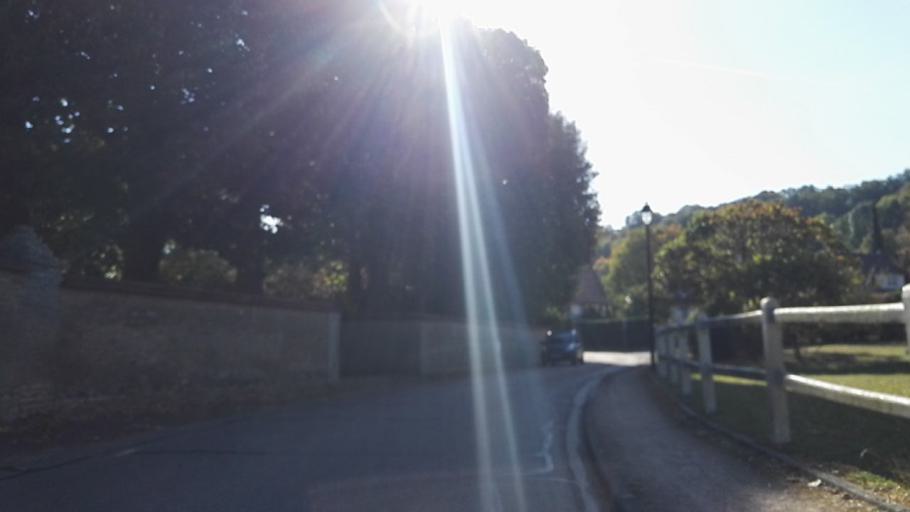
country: FR
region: Haute-Normandie
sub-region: Departement de l'Eure
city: Menilles
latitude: 49.0302
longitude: 1.3436
